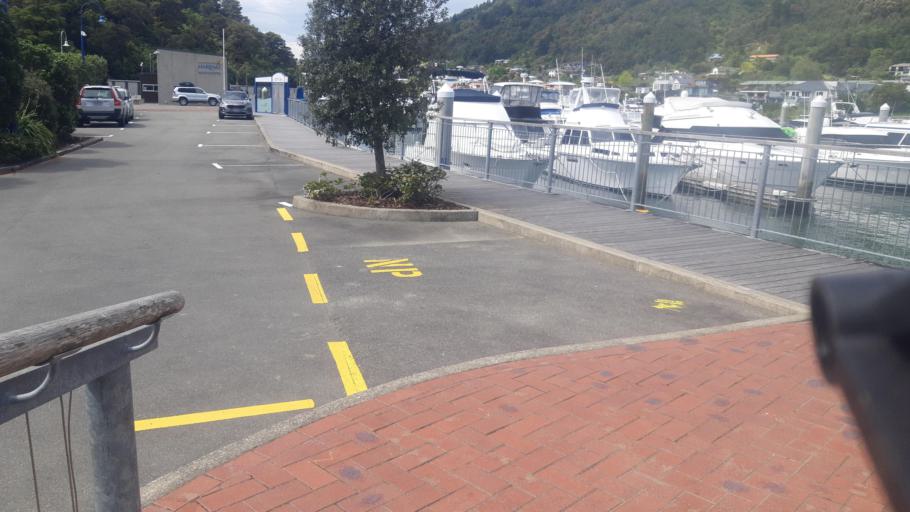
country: NZ
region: Marlborough
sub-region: Marlborough District
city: Picton
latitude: -41.2893
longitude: 174.0100
